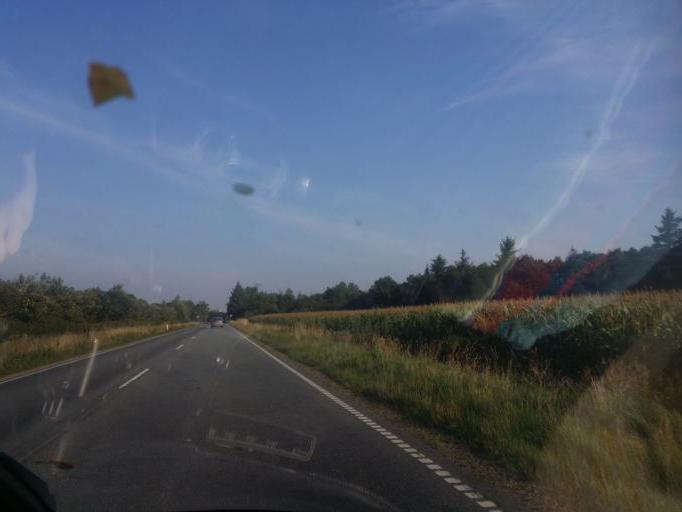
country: DK
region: South Denmark
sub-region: Tonder Kommune
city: Sherrebek
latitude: 55.1879
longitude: 8.7331
